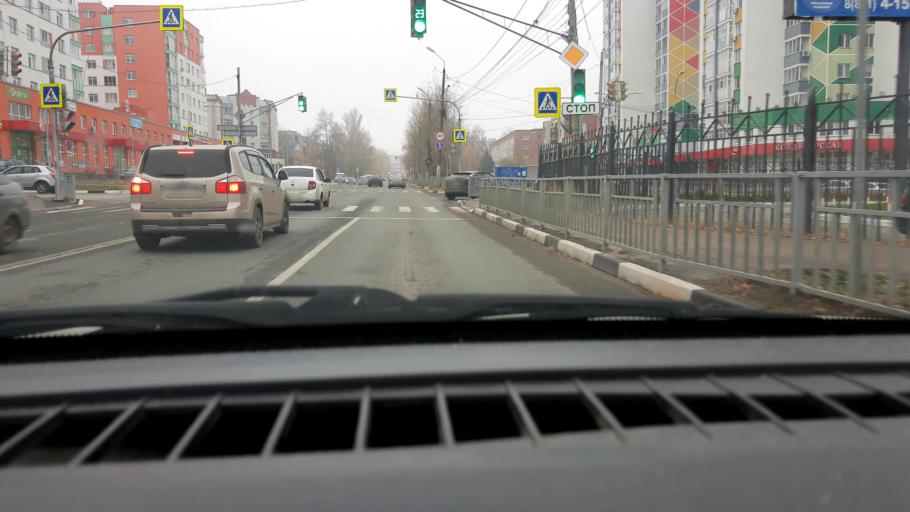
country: RU
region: Nizjnij Novgorod
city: Kstovo
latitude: 56.1517
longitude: 44.1882
